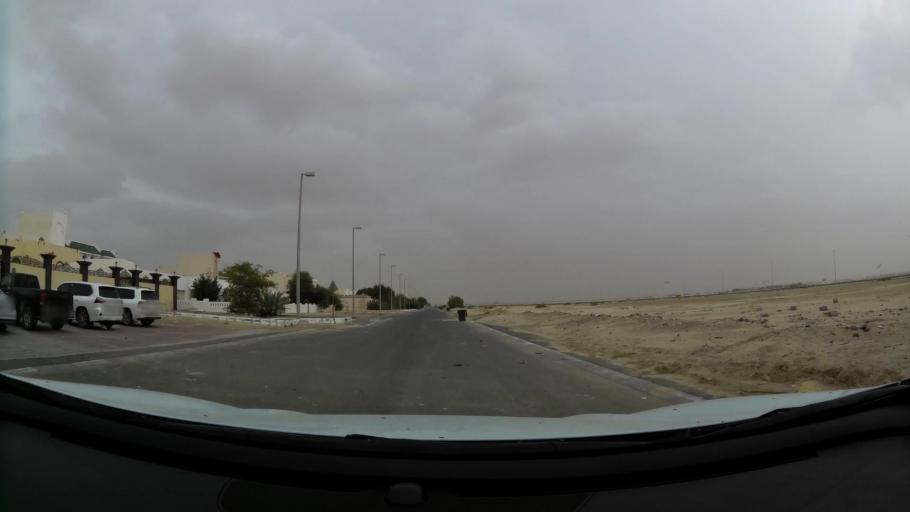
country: AE
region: Abu Dhabi
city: Abu Dhabi
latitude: 24.3664
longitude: 54.6679
